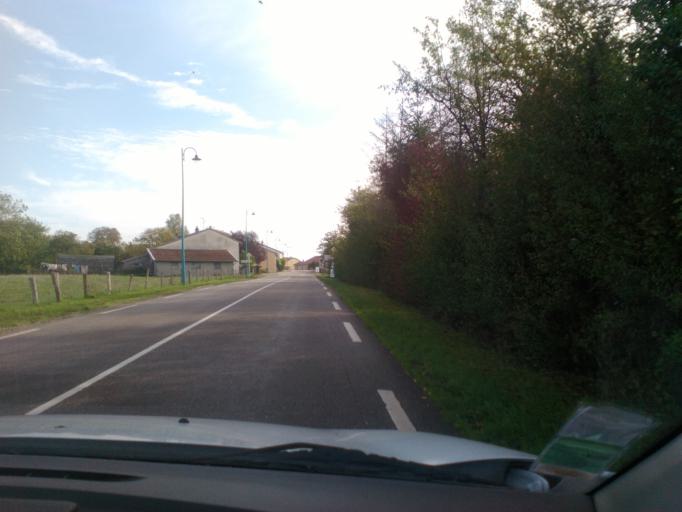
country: FR
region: Lorraine
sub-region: Departement des Vosges
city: Rambervillers
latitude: 48.3499
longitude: 6.5333
